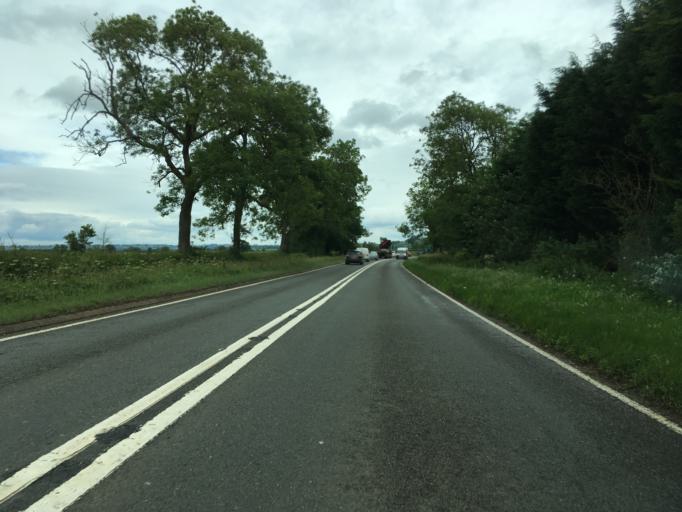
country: GB
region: England
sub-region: Warwickshire
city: Dunchurch
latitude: 52.2594
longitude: -1.3005
